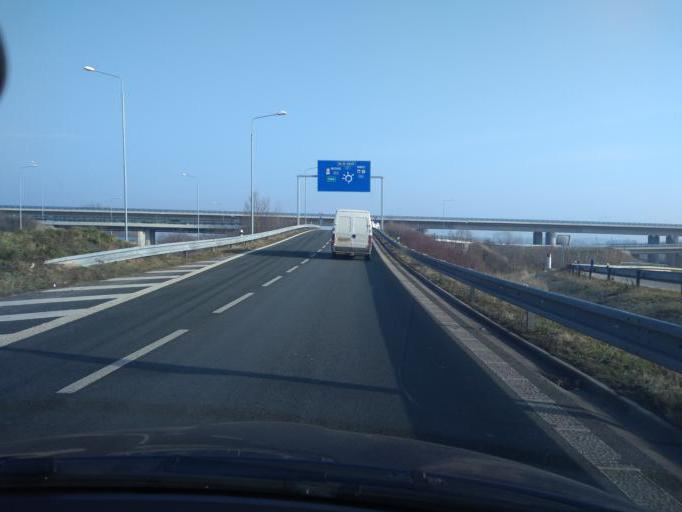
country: CZ
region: Pardubicky
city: Opatovice nad Labem
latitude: 50.1374
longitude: 15.7879
